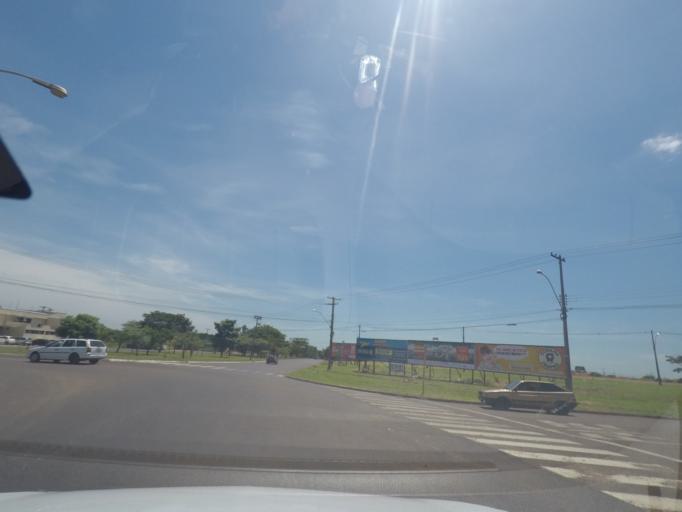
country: BR
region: Sao Paulo
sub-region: Matao
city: Matao
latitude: -21.6200
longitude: -48.3564
